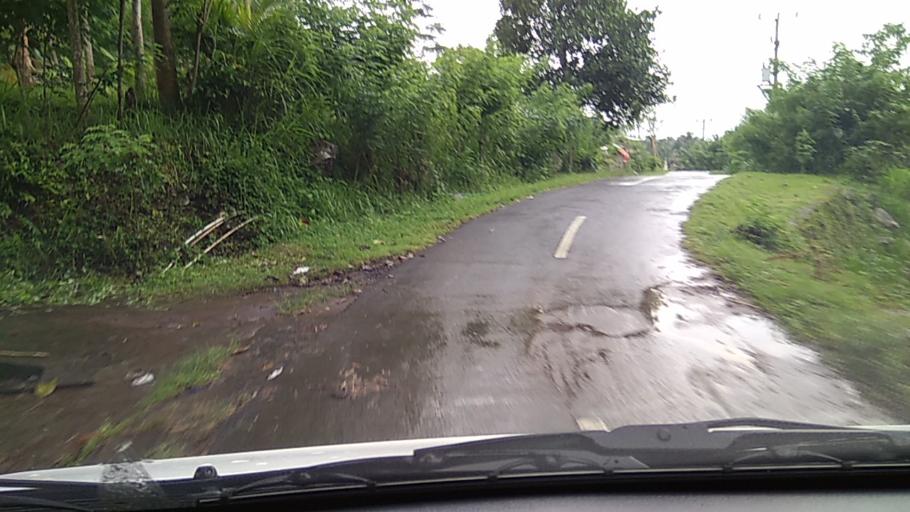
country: ID
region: Bali
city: Tiyingtali Kelod
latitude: -8.4061
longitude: 115.6271
